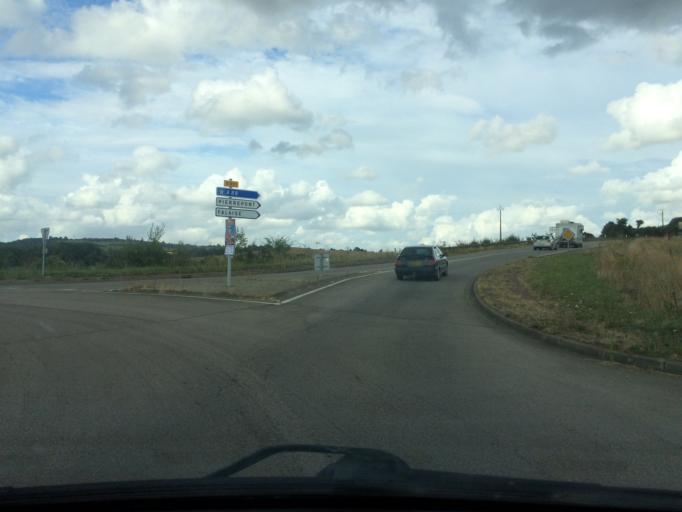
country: FR
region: Lower Normandy
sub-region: Departement du Calvados
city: Clecy
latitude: 48.8805
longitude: -0.4093
